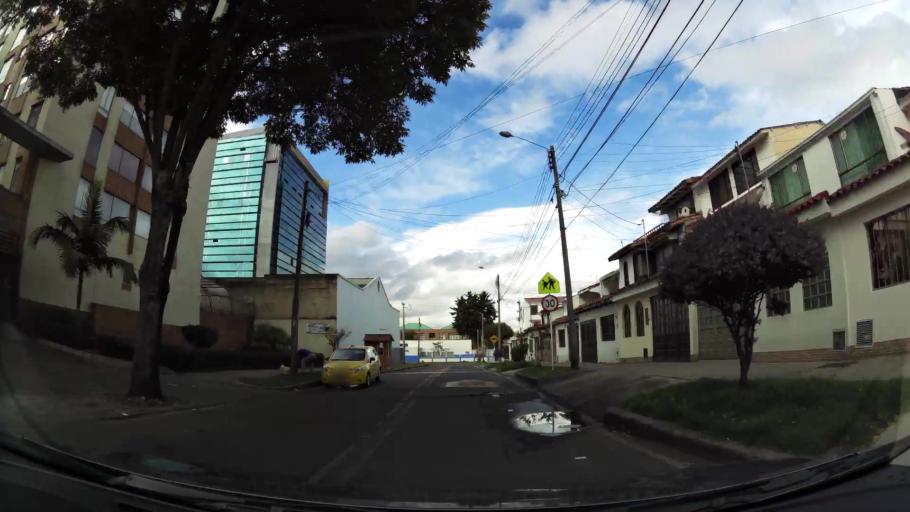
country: CO
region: Bogota D.C.
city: Barrio San Luis
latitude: 4.6879
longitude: -74.0764
